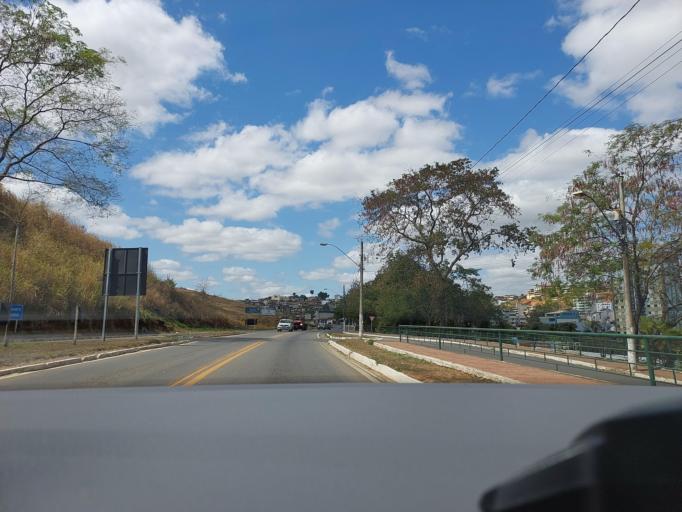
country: BR
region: Minas Gerais
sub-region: Muriae
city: Muriae
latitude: -21.1286
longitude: -42.3632
